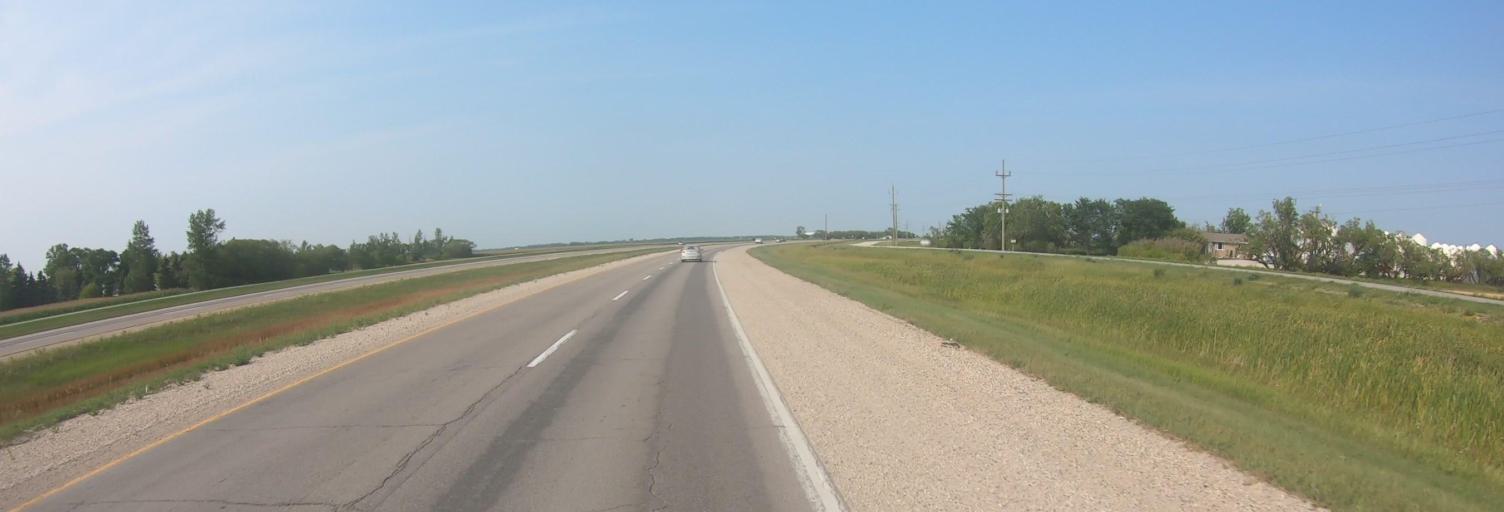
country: CA
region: Manitoba
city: Steinbach
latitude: 49.6371
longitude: -96.6868
